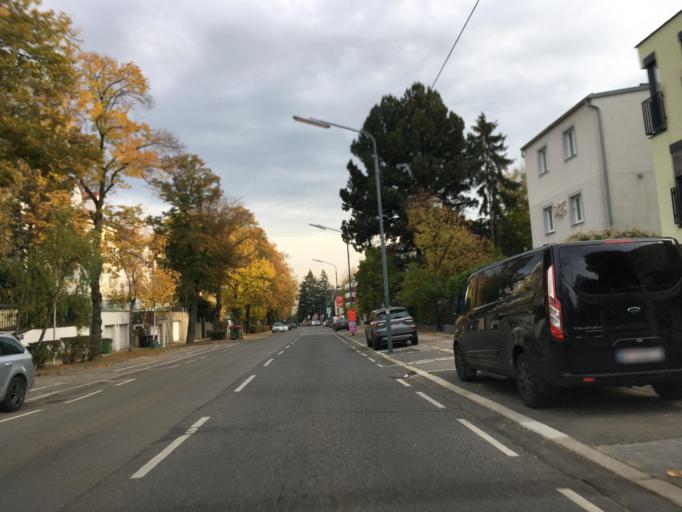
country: AT
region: Lower Austria
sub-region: Politischer Bezirk Wien-Umgebung
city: Klosterneuburg
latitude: 48.2490
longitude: 16.3098
